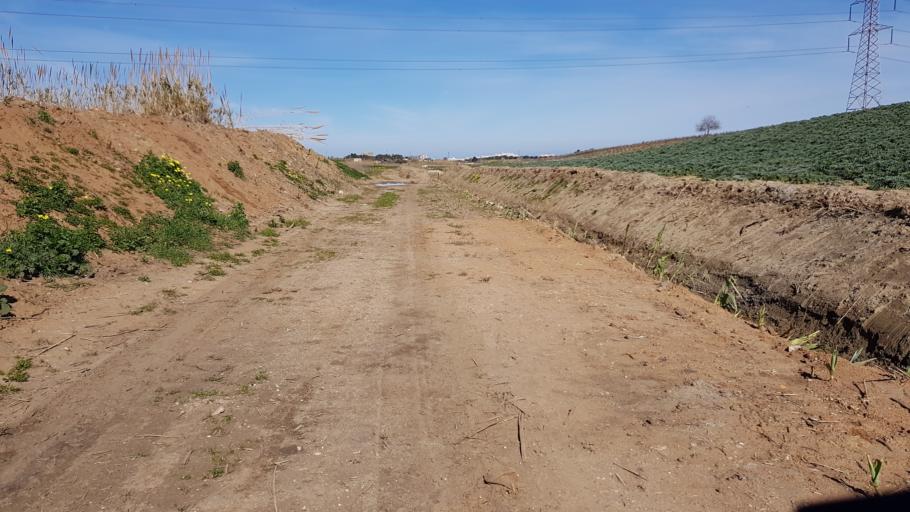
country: IT
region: Apulia
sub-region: Provincia di Brindisi
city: La Rosa
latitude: 40.5980
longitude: 17.9282
